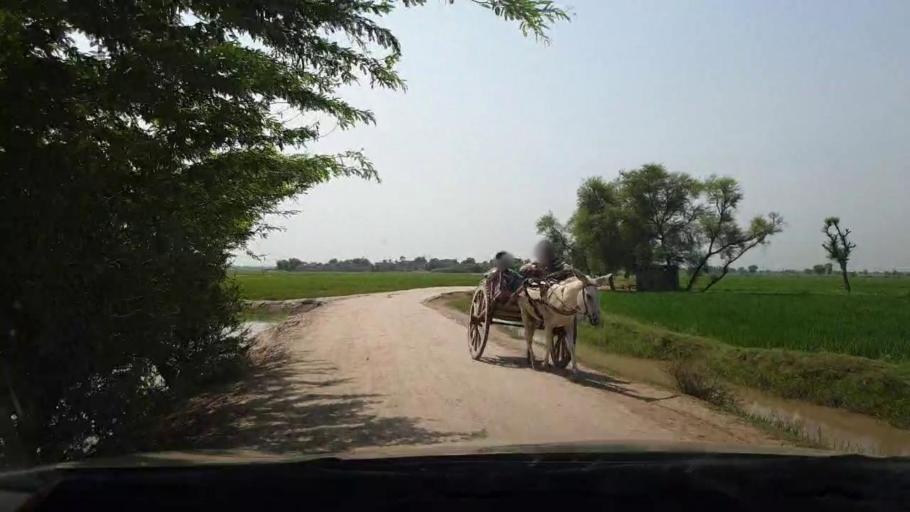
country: PK
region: Sindh
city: Naudero
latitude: 27.6524
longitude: 68.2595
